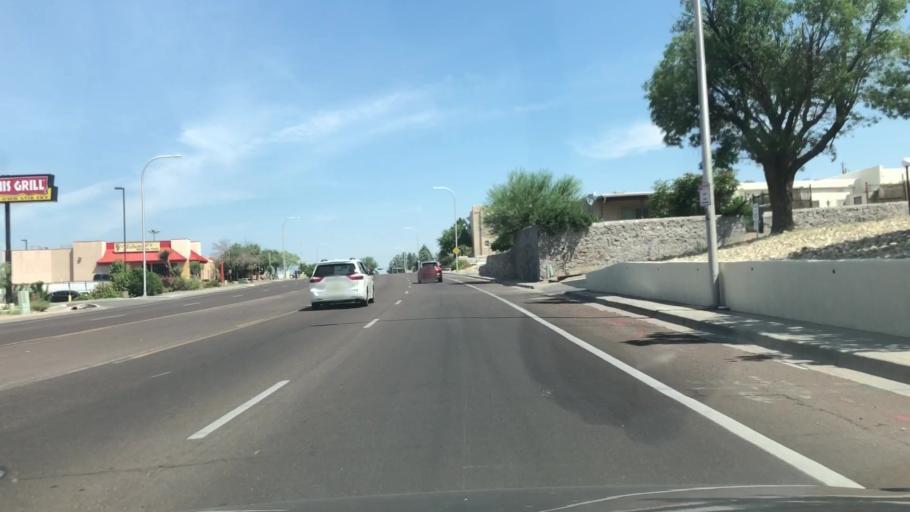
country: US
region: New Mexico
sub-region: Dona Ana County
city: University Park
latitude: 32.3073
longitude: -106.7389
